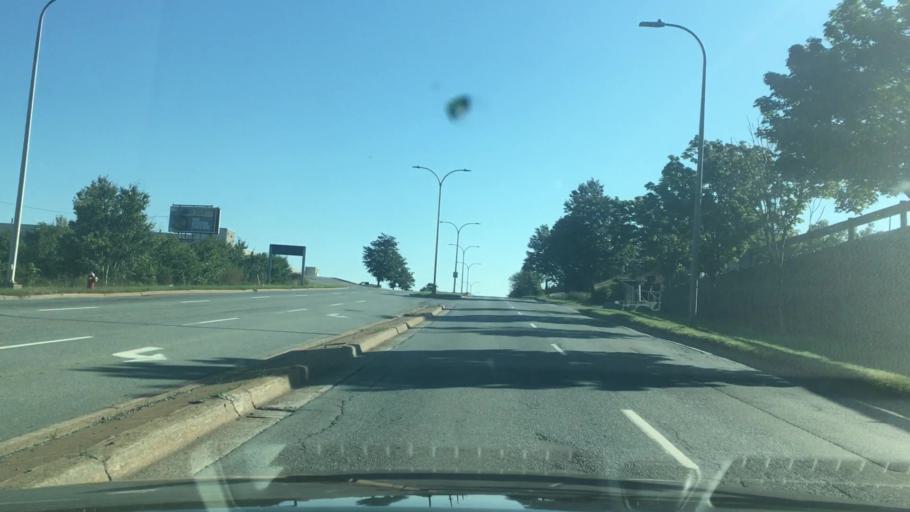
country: CA
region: Nova Scotia
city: Dartmouth
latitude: 44.7117
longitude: -63.5992
